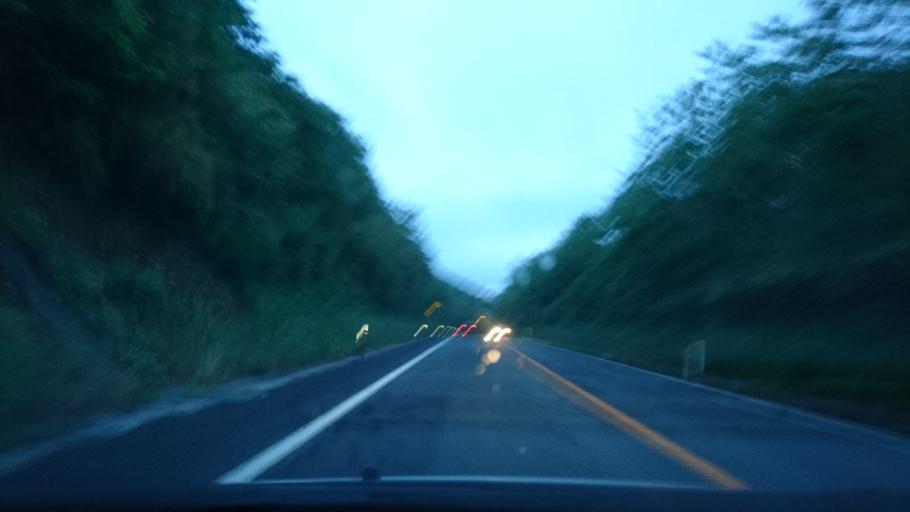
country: JP
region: Iwate
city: Ichinoseki
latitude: 38.8430
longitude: 141.0937
